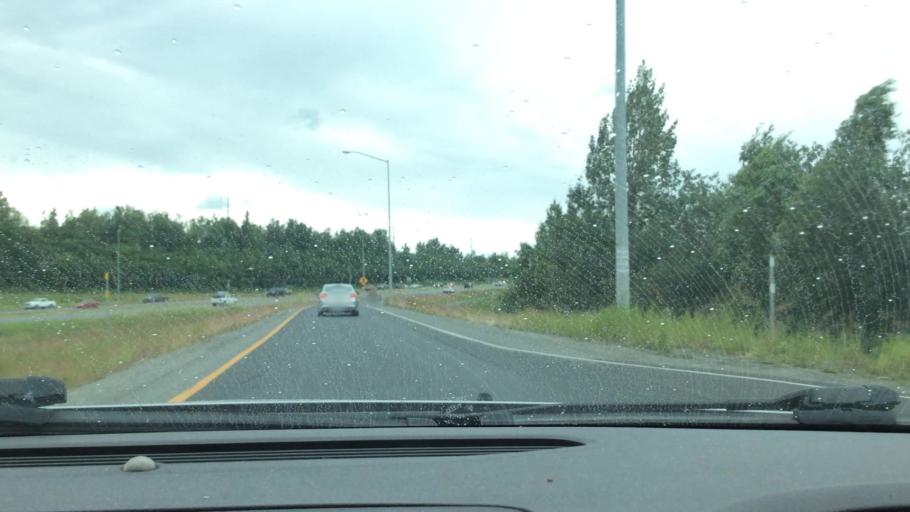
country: US
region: Alaska
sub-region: Anchorage Municipality
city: Elmendorf Air Force Base
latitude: 61.2539
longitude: -149.6618
